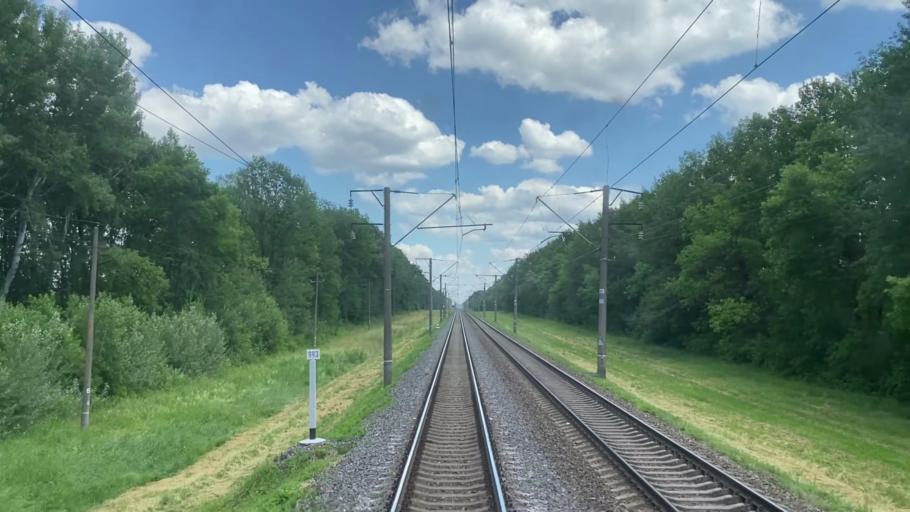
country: BY
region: Brest
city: Byaroza
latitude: 52.5415
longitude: 24.9416
